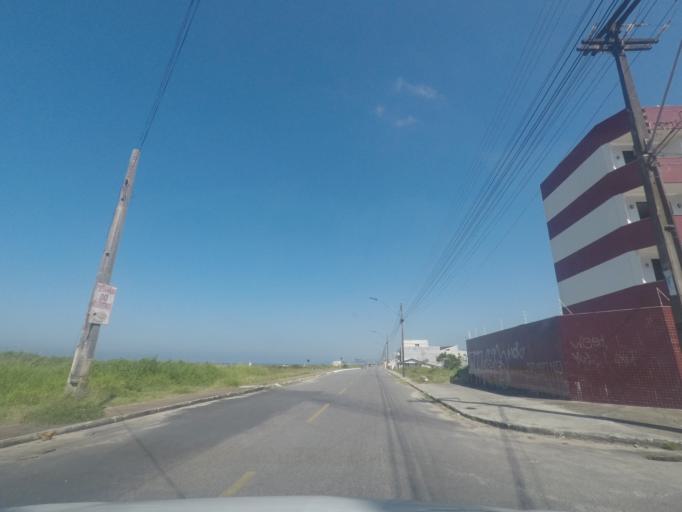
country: BR
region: Parana
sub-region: Pontal Do Parana
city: Pontal do Parana
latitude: -25.7410
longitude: -48.4949
